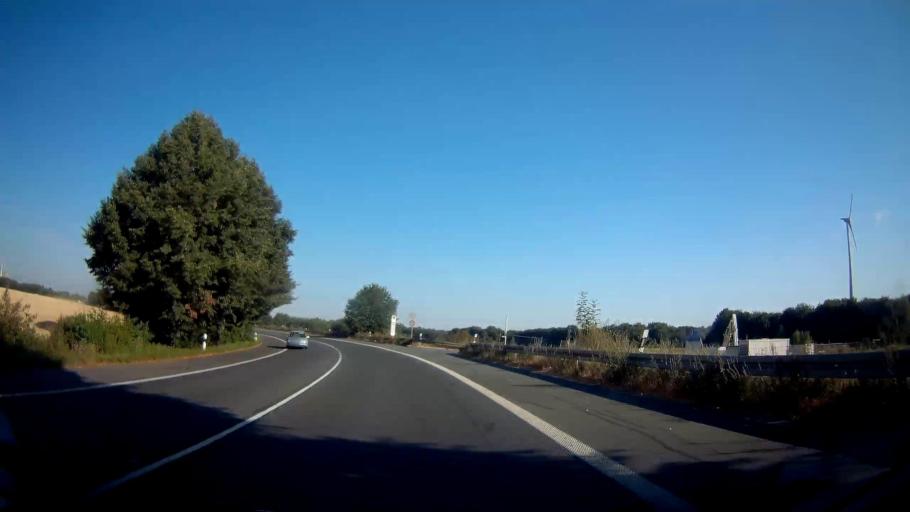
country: DE
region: North Rhine-Westphalia
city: Waltrop
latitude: 51.5625
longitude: 7.4106
